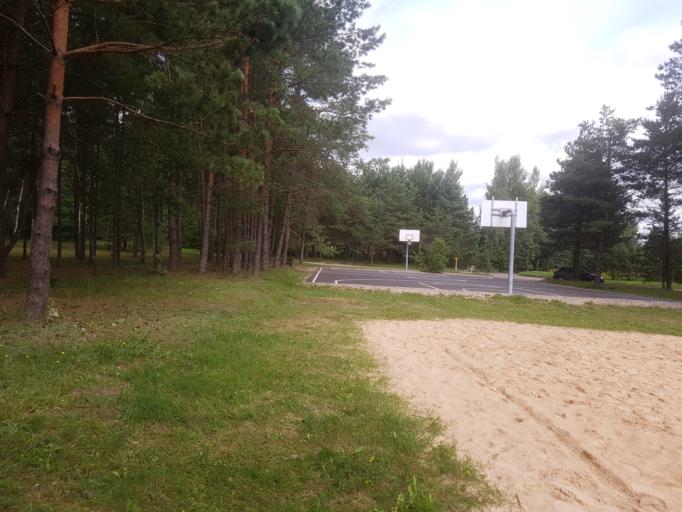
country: LT
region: Vilnius County
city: Rasos
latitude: 54.7829
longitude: 25.3400
